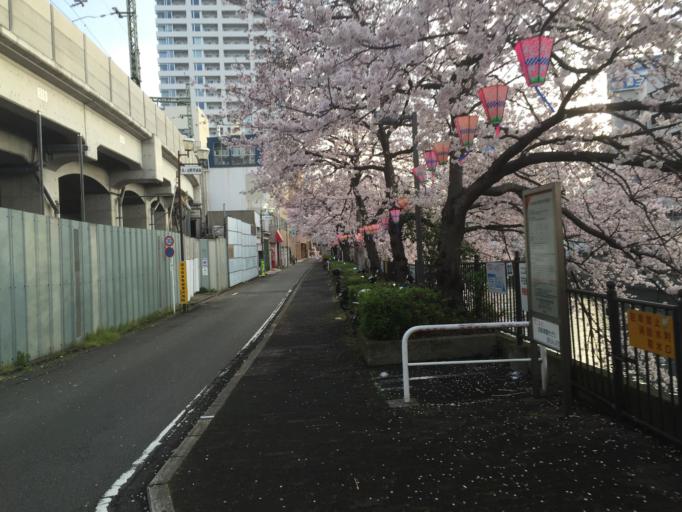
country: JP
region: Kanagawa
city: Yokohama
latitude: 35.4438
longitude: 139.6269
